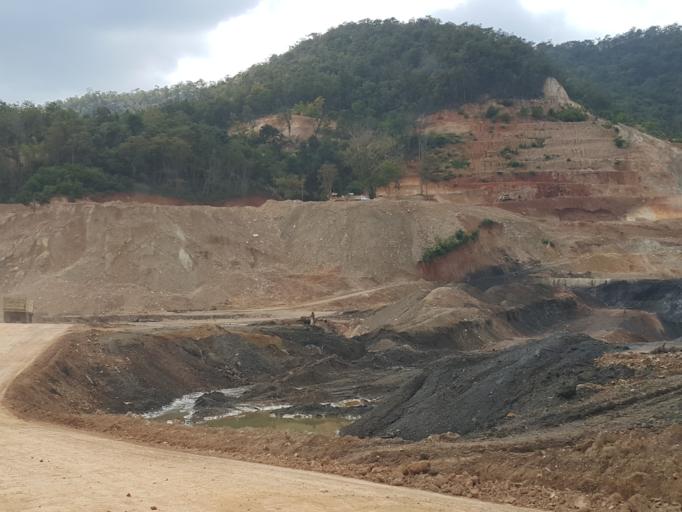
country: TH
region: Lampang
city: Chae Hom
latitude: 18.5733
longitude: 99.4396
